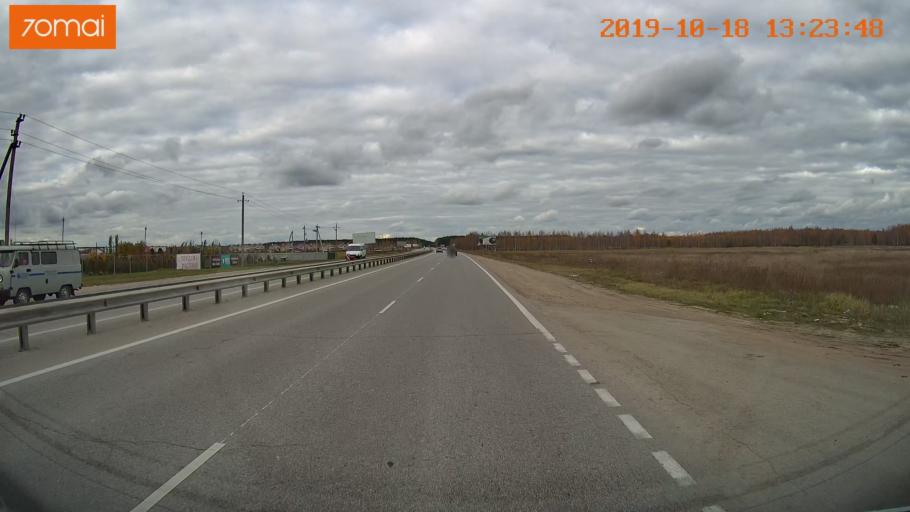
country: RU
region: Rjazan
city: Polyany
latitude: 54.7218
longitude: 39.8473
